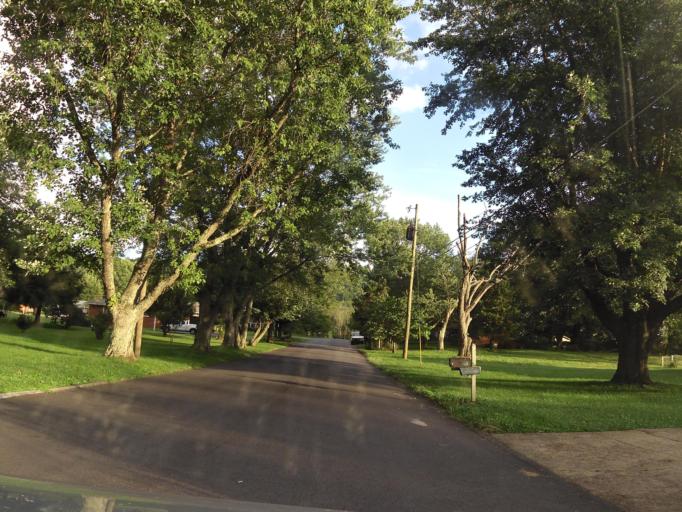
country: US
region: Tennessee
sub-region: Knox County
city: Knoxville
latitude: 35.9985
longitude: -83.9982
